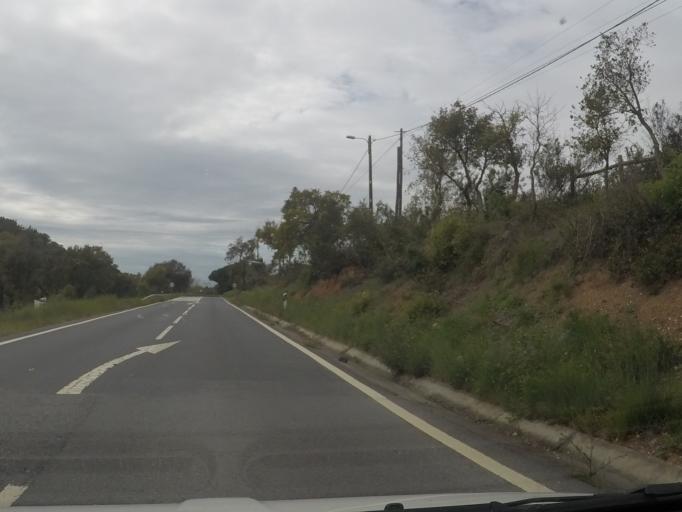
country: PT
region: Setubal
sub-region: Sines
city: Porto Covo
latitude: 37.8671
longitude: -8.7340
